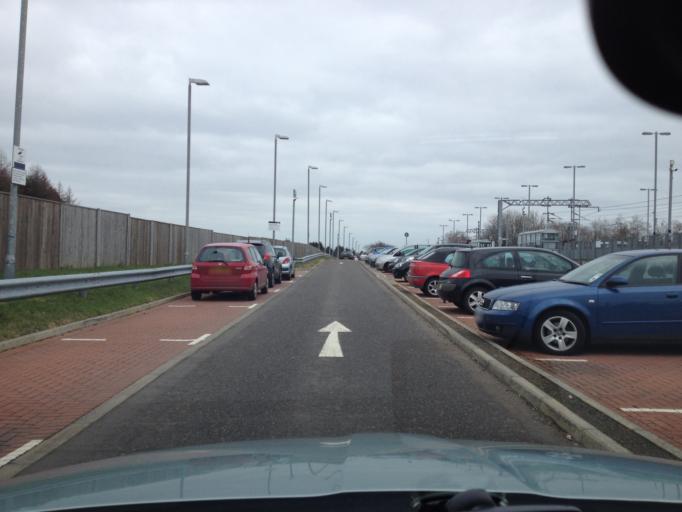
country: GB
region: Scotland
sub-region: West Lothian
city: Livingston
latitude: 55.9193
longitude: -3.5027
